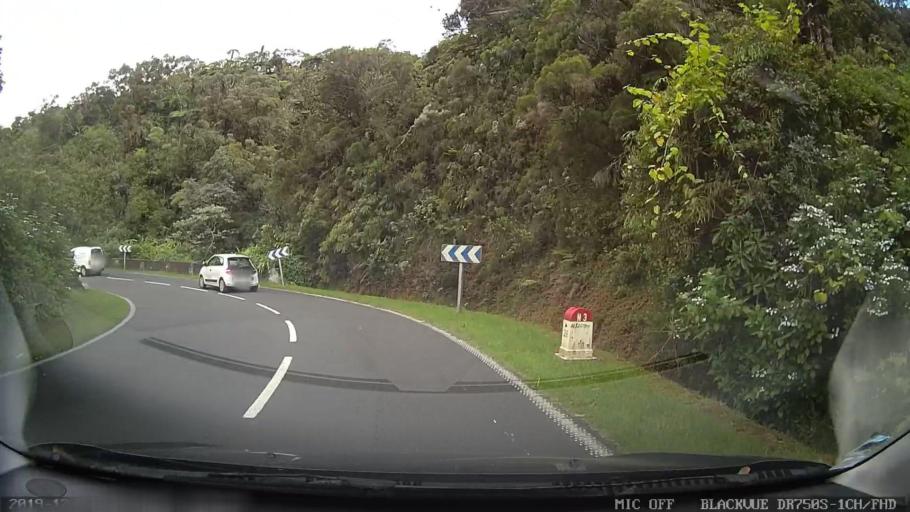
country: RE
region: Reunion
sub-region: Reunion
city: Cilaos
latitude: -21.1614
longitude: 55.5950
